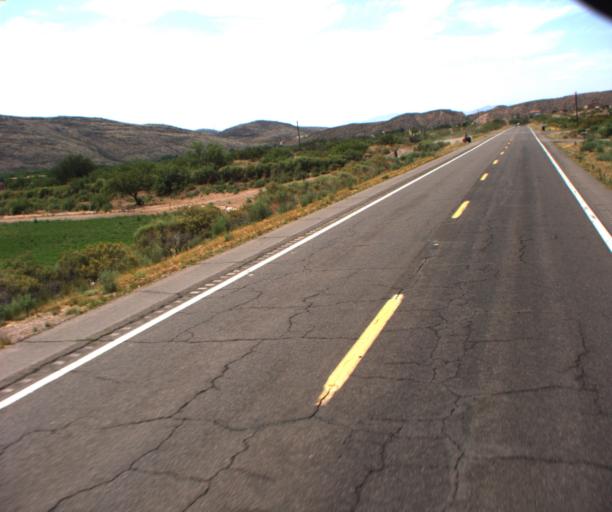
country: US
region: Arizona
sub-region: Greenlee County
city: Clifton
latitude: 32.8614
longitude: -109.1852
